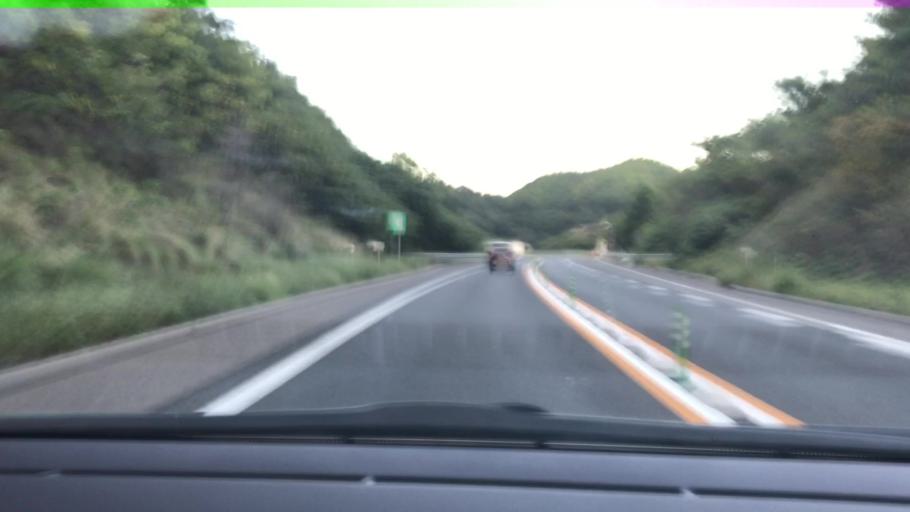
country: JP
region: Hiroshima
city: Innoshima
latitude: 34.3278
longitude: 133.1521
